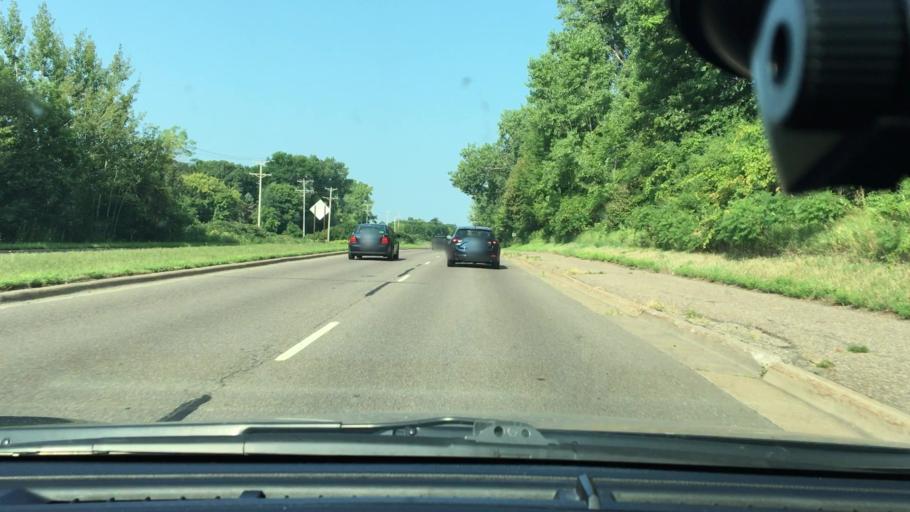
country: US
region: Minnesota
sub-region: Hennepin County
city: New Hope
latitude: 45.0333
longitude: -93.4114
